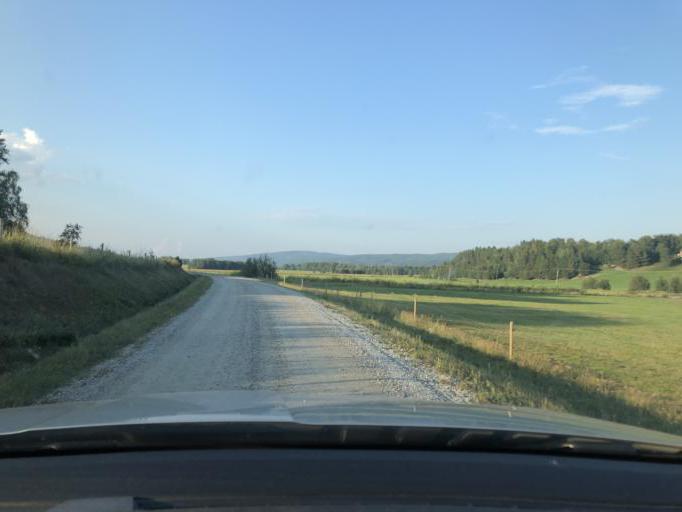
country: SE
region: Vaesternorrland
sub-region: Kramfors Kommun
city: Bollstabruk
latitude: 63.0648
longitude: 17.7344
